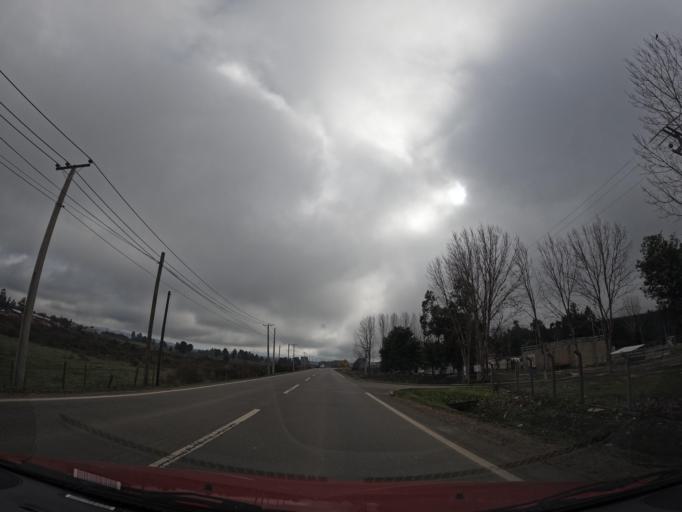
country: CL
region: Maule
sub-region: Provincia de Cauquenes
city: Cauquenes
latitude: -36.2695
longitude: -72.5465
